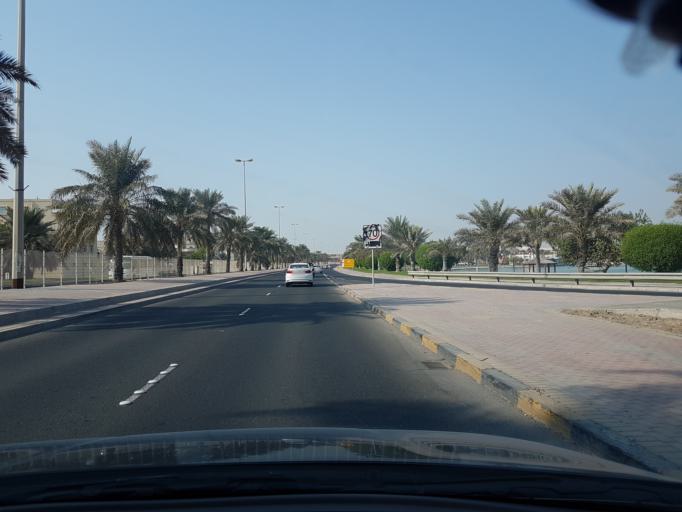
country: BH
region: Muharraq
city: Al Muharraq
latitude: 26.2585
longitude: 50.6222
